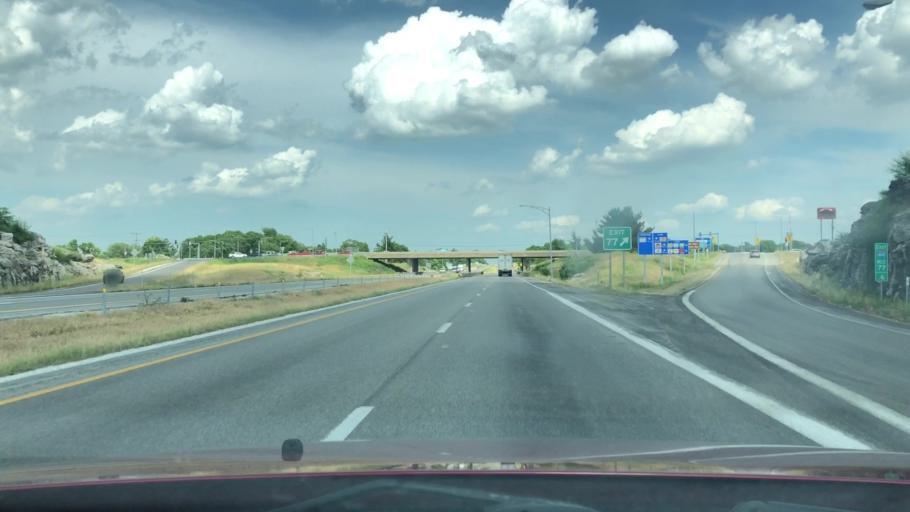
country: US
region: Missouri
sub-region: Greene County
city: Springfield
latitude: 37.2502
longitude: -93.3138
